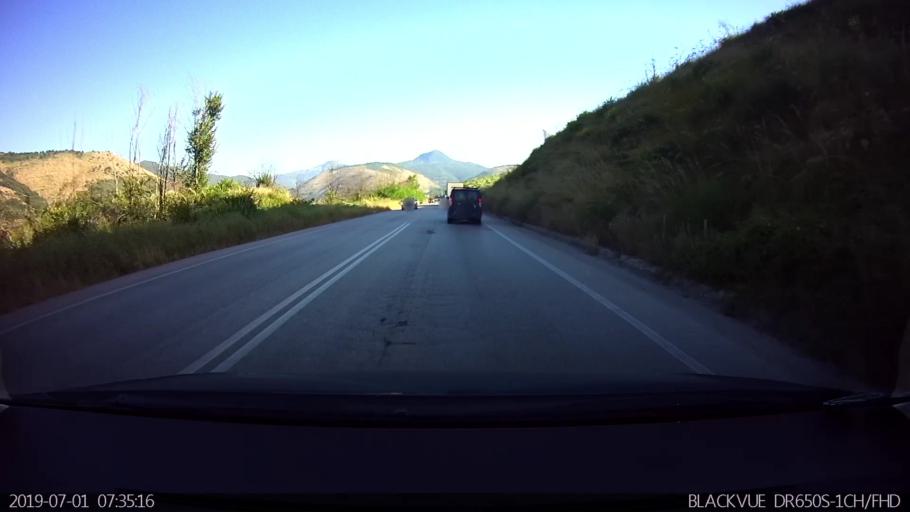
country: IT
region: Latium
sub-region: Provincia di Latina
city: Prossedi
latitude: 41.5231
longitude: 13.2710
